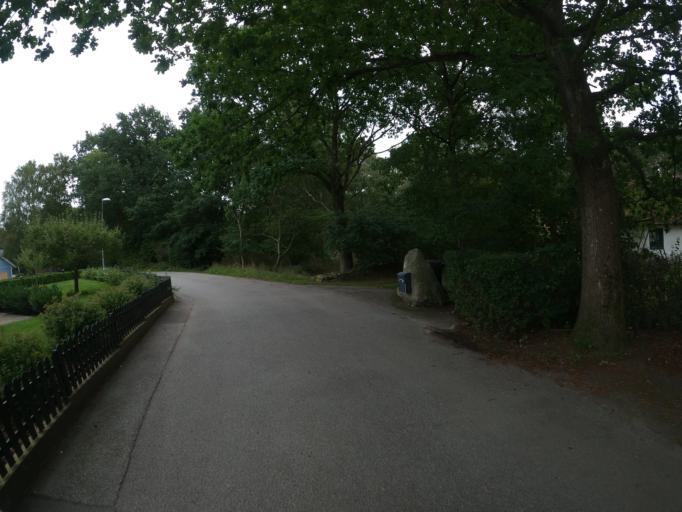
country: SE
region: Skane
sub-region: Lunds Kommun
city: Genarp
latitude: 55.5953
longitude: 13.4096
